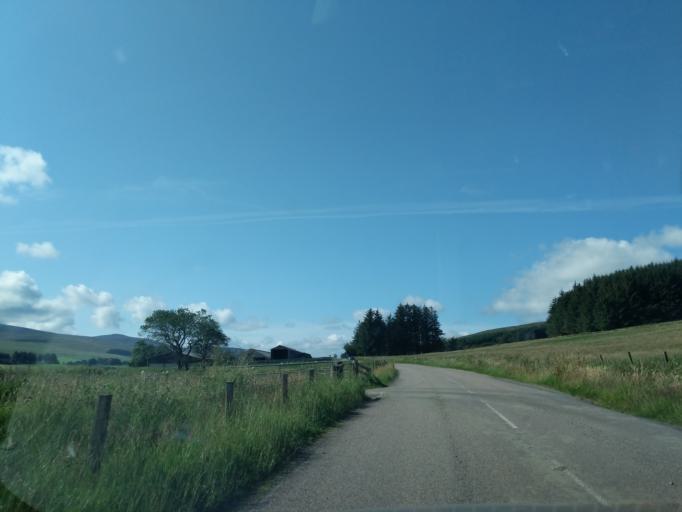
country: GB
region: Scotland
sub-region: Moray
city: Dufftown
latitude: 57.3908
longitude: -3.2129
